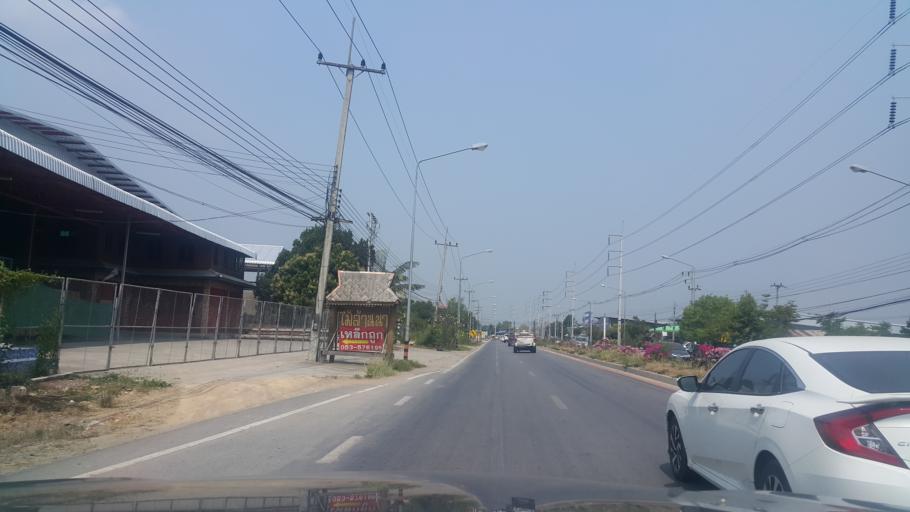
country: TH
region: Lamphun
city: Pa Sang
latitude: 18.4801
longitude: 98.9461
